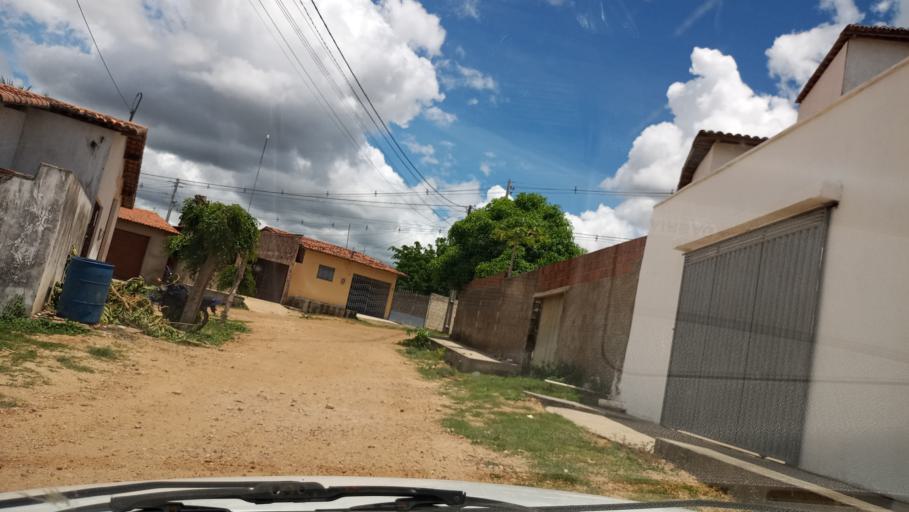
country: BR
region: Rio Grande do Norte
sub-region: Sao Paulo Do Potengi
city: Sao Paulo do Potengi
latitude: -5.9011
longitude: -35.7726
